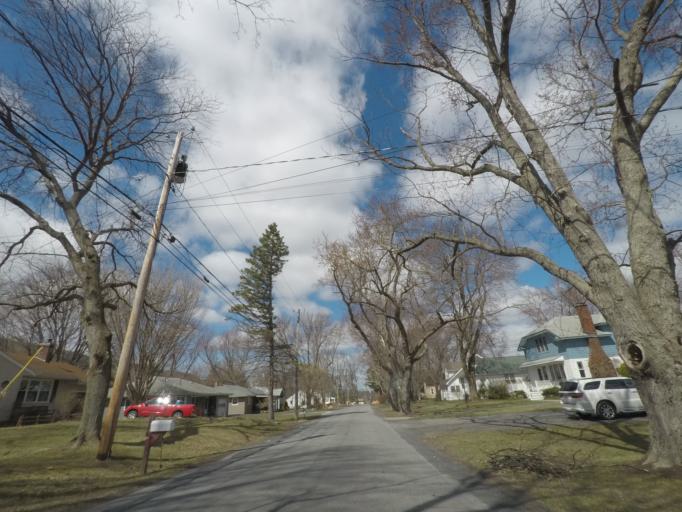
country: US
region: New York
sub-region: Albany County
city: Voorheesville
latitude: 42.6199
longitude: -73.9676
